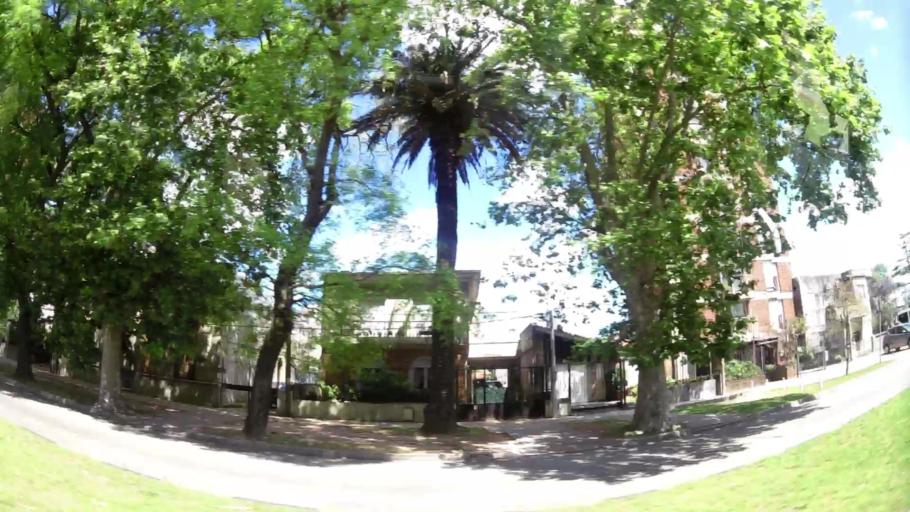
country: UY
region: Montevideo
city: Montevideo
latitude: -34.8724
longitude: -56.1965
